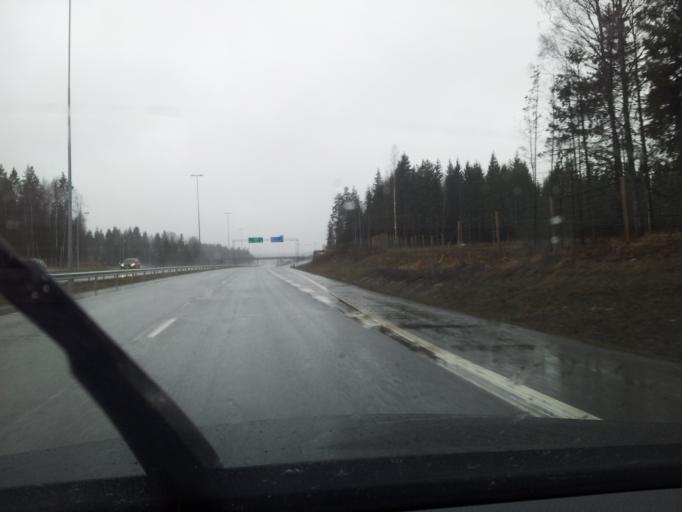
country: FI
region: Uusimaa
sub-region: Helsinki
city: Kirkkonummi
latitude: 60.1391
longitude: 24.5432
